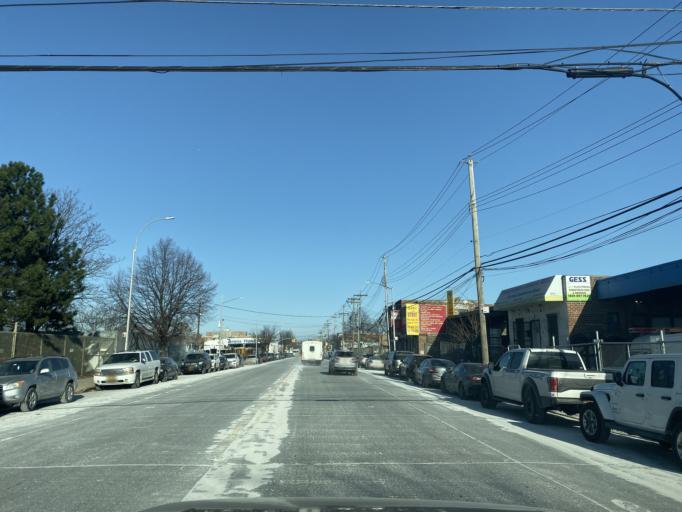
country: US
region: New York
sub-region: Bronx
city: The Bronx
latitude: 40.8299
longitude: -73.8442
